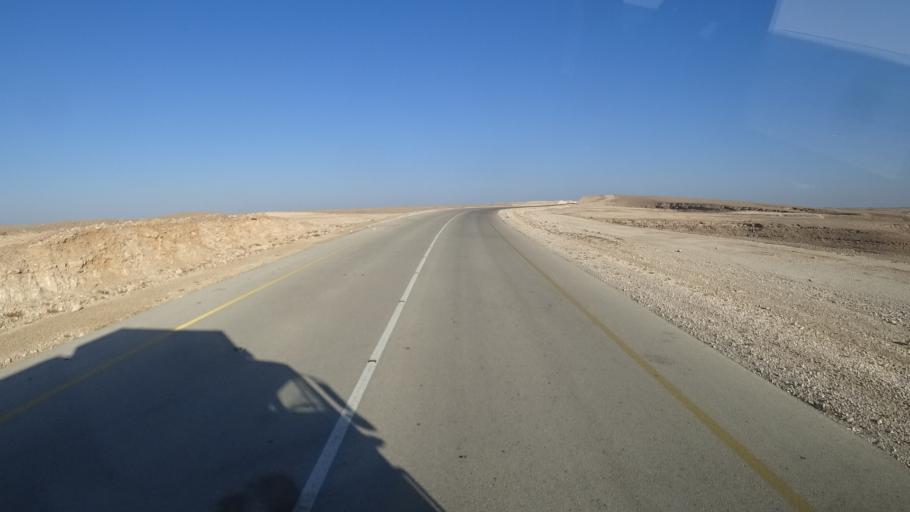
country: YE
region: Al Mahrah
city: Hawf
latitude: 17.0867
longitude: 53.0760
